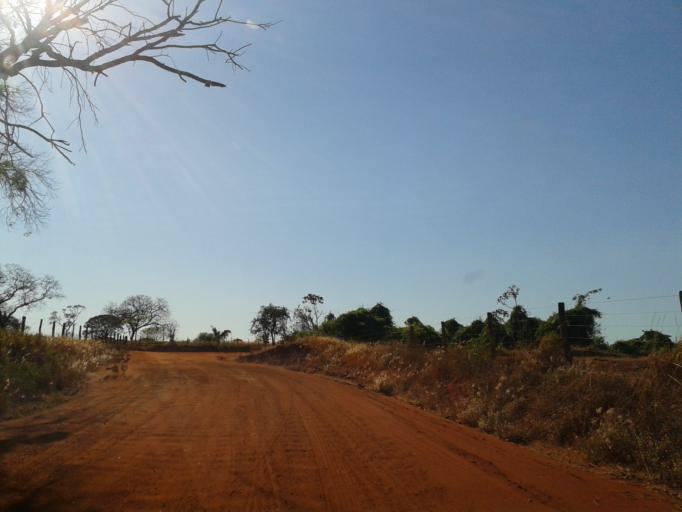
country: BR
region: Minas Gerais
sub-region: Ituiutaba
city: Ituiutaba
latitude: -18.9820
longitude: -49.3994
